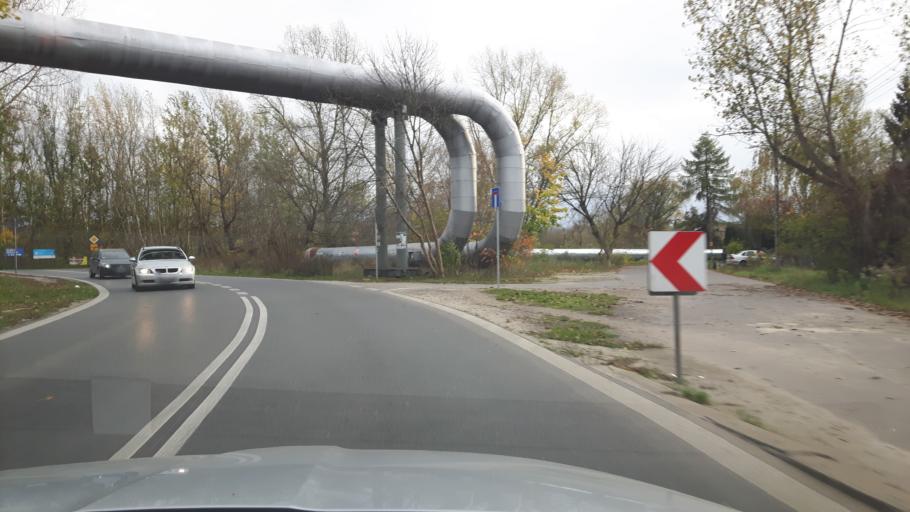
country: PL
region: Masovian Voivodeship
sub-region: Powiat wolominski
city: Zabki
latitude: 52.2750
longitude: 21.0876
